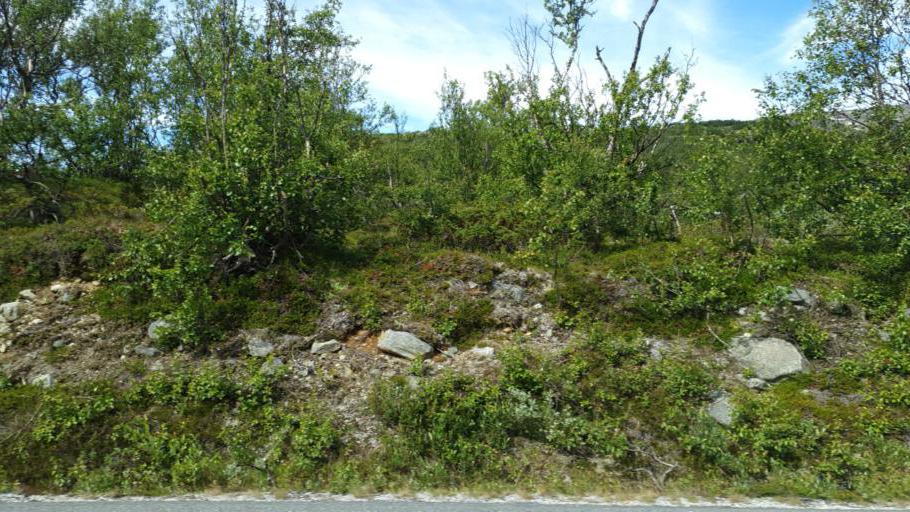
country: NO
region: Oppland
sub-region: Oystre Slidre
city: Heggenes
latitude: 61.4924
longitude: 8.8424
